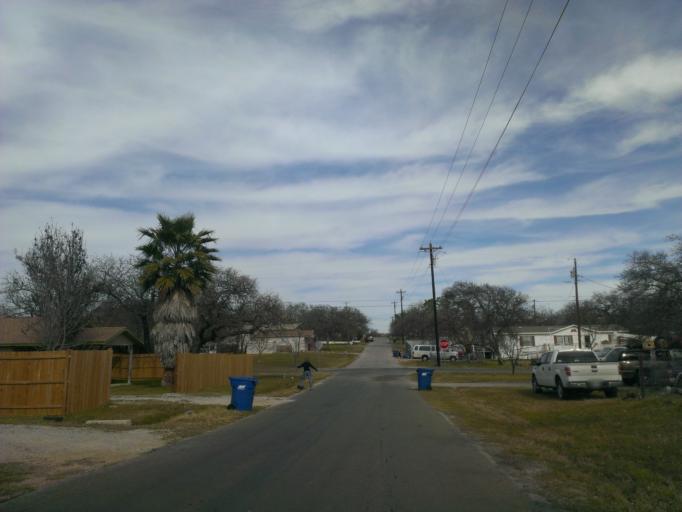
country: US
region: Texas
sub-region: Burnet County
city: Granite Shoals
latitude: 30.5905
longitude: -98.3816
